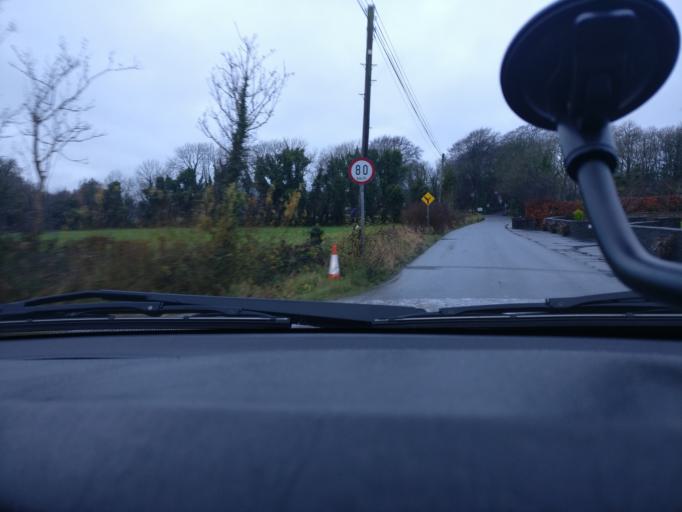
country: IE
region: Connaught
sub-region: County Galway
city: Loughrea
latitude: 53.2496
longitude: -8.5583
